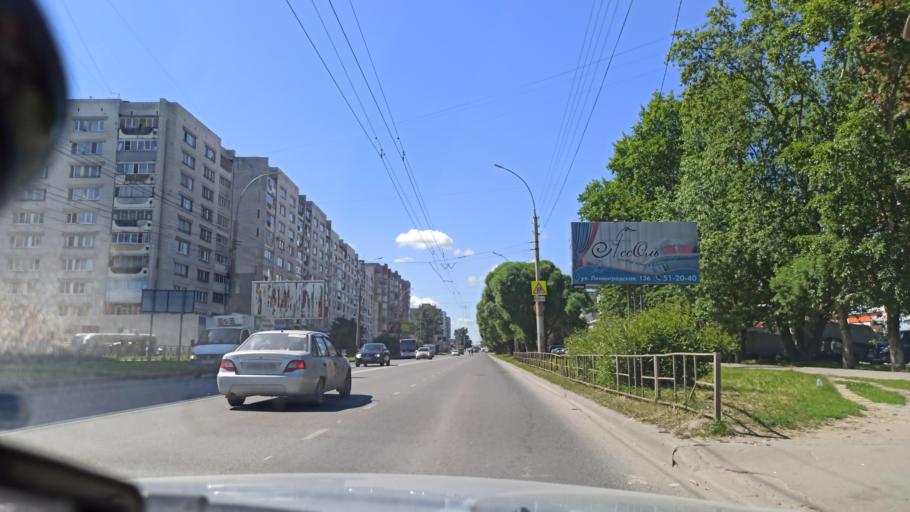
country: RU
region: Vologda
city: Vologda
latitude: 59.2043
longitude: 39.8352
